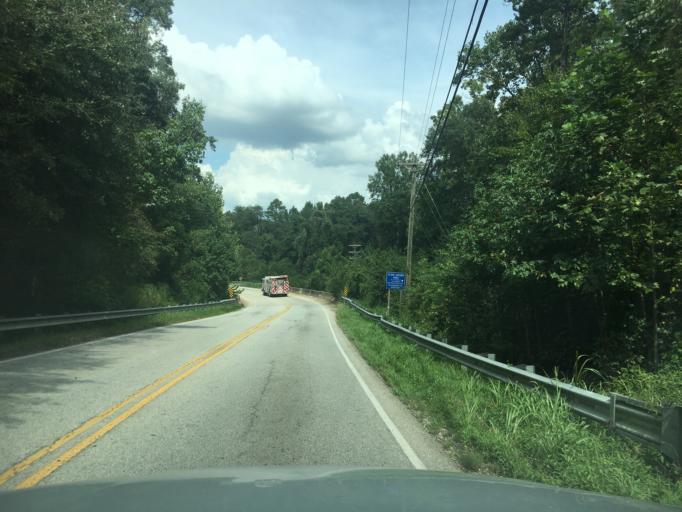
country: US
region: South Carolina
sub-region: Greenville County
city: Five Forks
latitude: 34.8443
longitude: -82.2259
